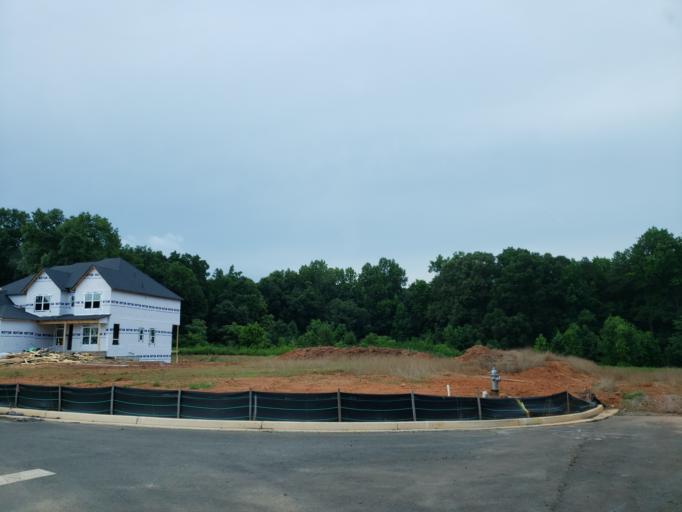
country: US
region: Georgia
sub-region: Cherokee County
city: Holly Springs
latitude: 34.1825
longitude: -84.4256
